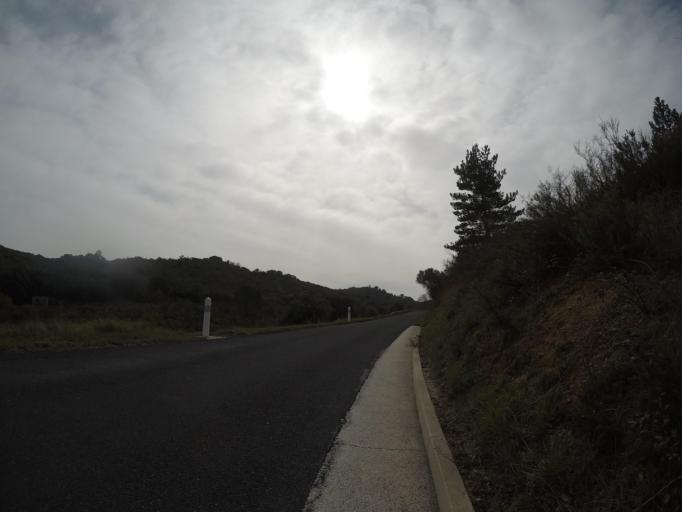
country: FR
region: Languedoc-Roussillon
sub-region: Departement des Pyrenees-Orientales
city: Estagel
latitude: 42.7485
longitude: 2.7239
